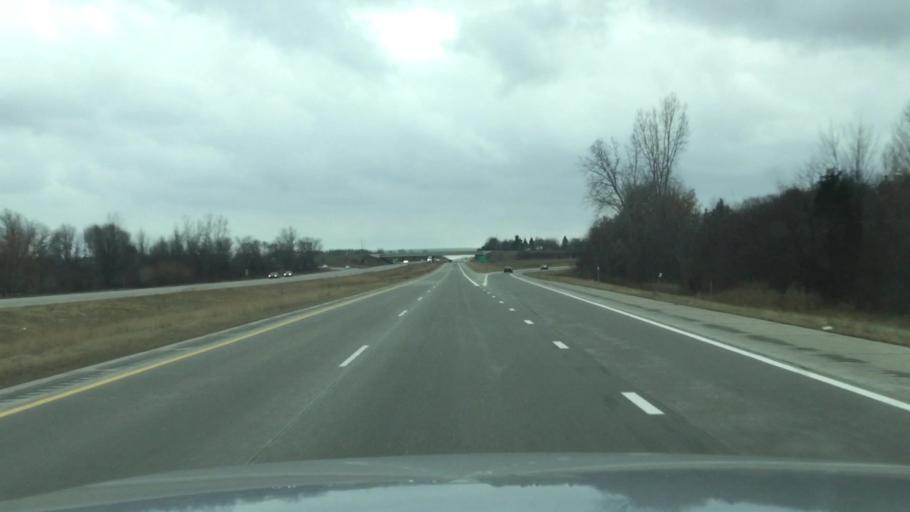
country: US
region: Michigan
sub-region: Genesee County
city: Grand Blanc
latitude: 42.9499
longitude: -83.6822
